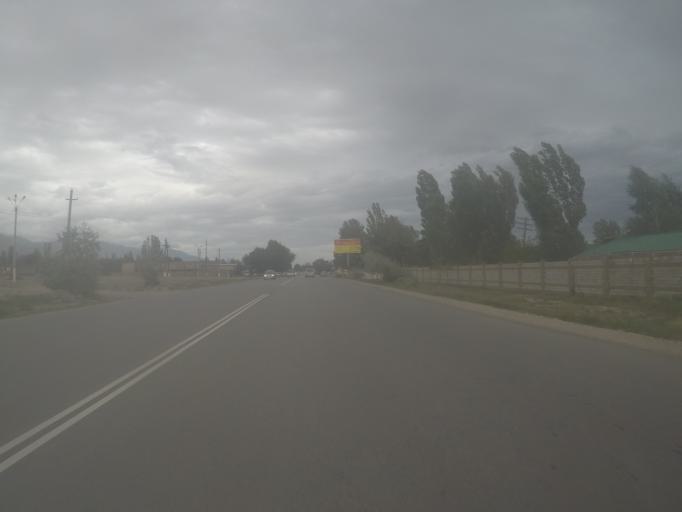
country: KG
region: Ysyk-Koel
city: Cholpon-Ata
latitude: 42.5843
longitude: 76.7339
